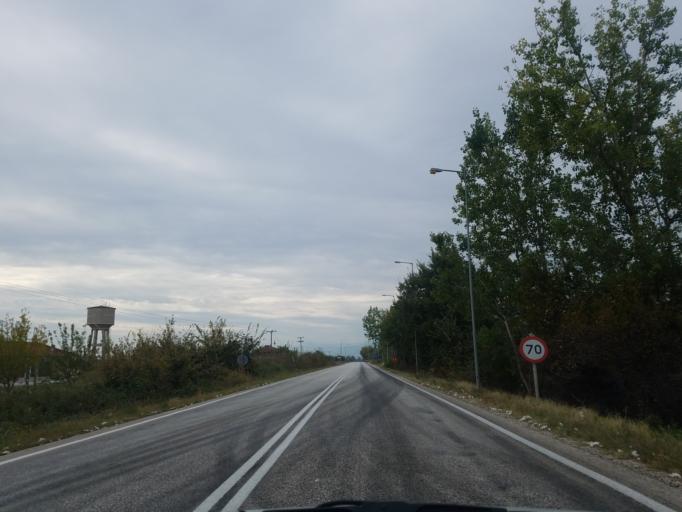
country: GR
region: Thessaly
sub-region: Nomos Kardhitsas
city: Agnantero
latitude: 39.4942
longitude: 21.8385
